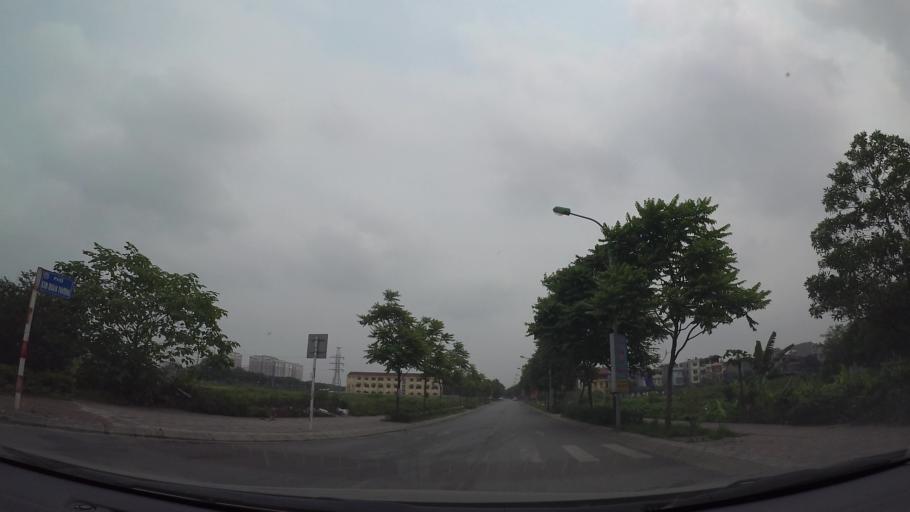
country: VN
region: Ha Noi
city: Trau Quy
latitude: 21.0622
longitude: 105.8999
